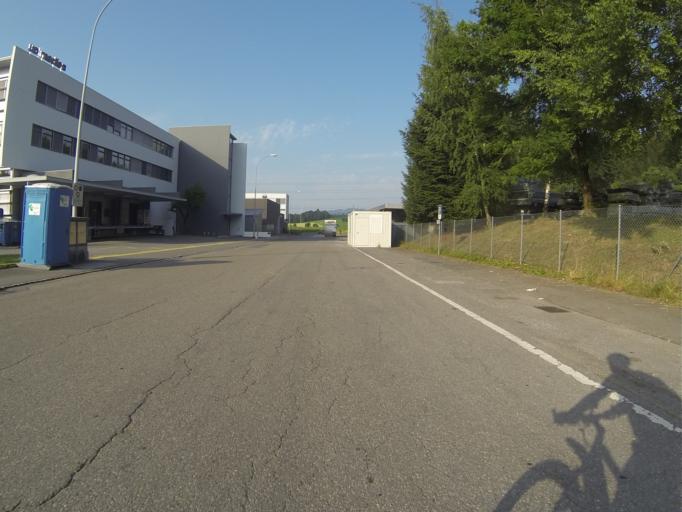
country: CH
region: Lucerne
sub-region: Hochdorf District
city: Emmen
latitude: 47.0650
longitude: 8.2902
